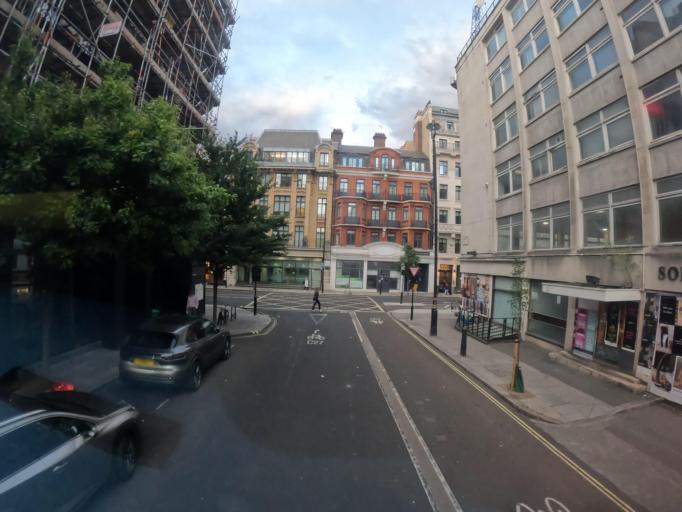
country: GB
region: England
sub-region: Greater London
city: Camden Town
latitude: 51.5224
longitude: -0.1442
